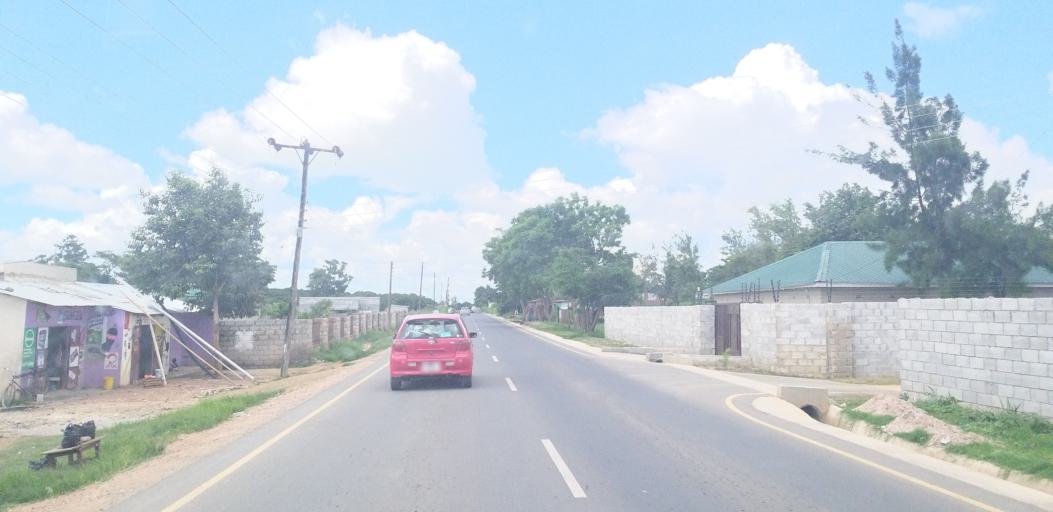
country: ZM
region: Lusaka
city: Lusaka
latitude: -15.3369
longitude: 28.3296
